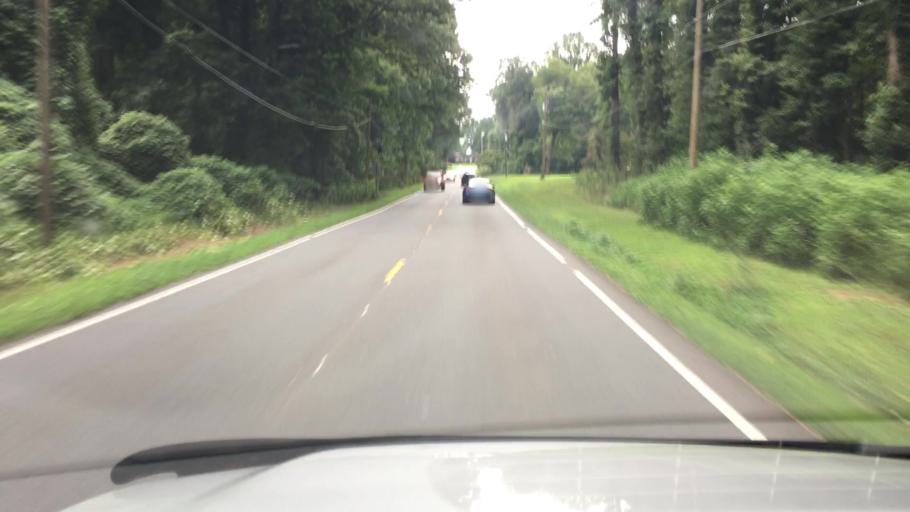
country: US
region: North Carolina
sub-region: Mecklenburg County
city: Huntersville
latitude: 35.3561
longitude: -80.8922
